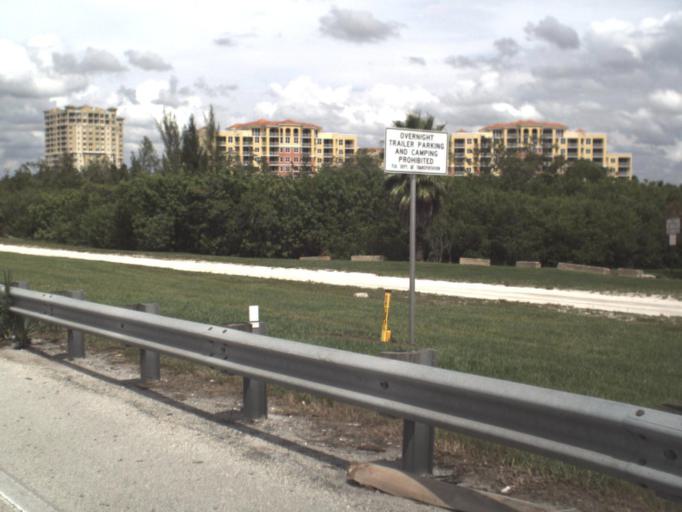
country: US
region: Florida
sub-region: Manatee County
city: Bradenton
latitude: 27.5075
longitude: -82.5630
